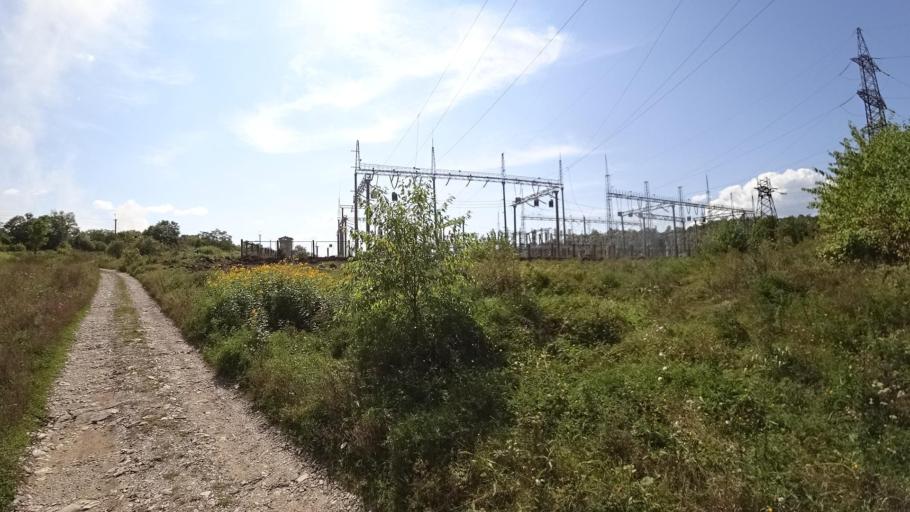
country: RU
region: Jewish Autonomous Oblast
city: Londoko
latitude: 49.0147
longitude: 131.8980
